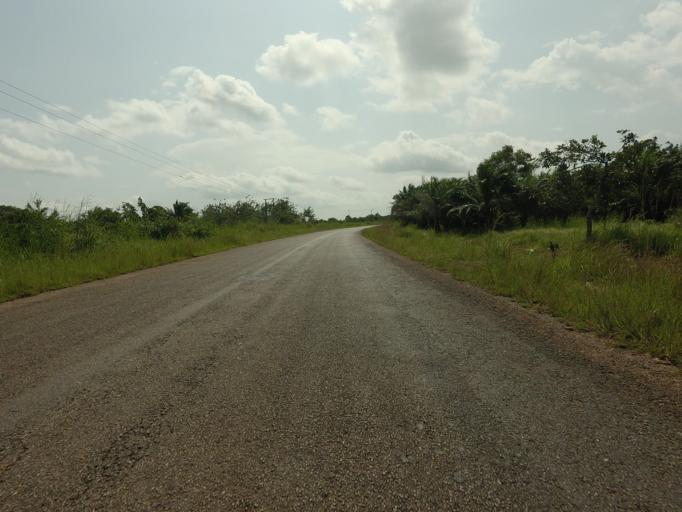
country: TG
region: Maritime
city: Lome
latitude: 6.2599
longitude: 0.9588
